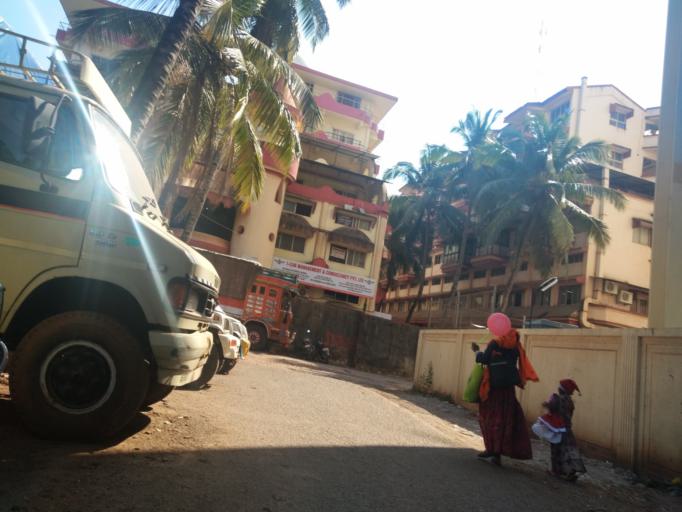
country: IN
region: Goa
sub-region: South Goa
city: Madgaon
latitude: 15.2850
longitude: 73.9579
